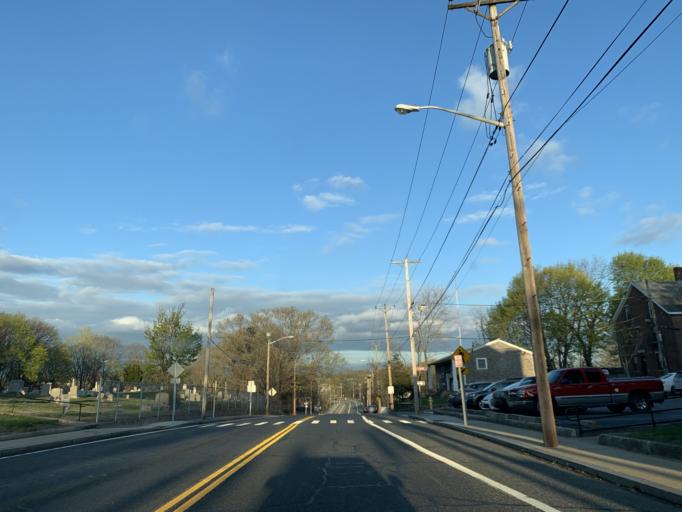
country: US
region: Rhode Island
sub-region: Providence County
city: Valley Falls
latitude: 41.9070
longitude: -71.4031
